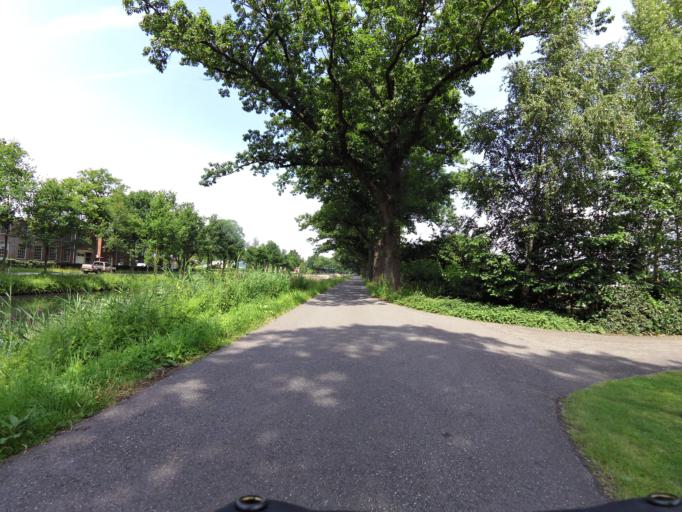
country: NL
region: Gelderland
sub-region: Gemeente Apeldoorn
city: Loenen
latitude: 52.1315
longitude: 6.0443
